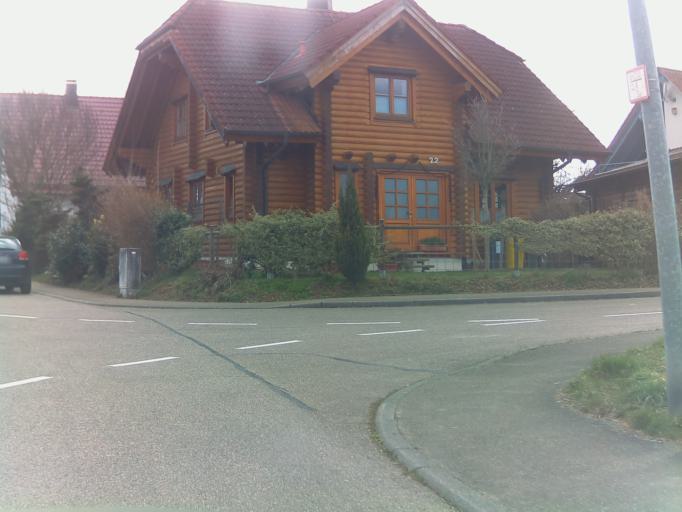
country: DE
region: Baden-Wuerttemberg
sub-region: Regierungsbezirk Stuttgart
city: Alfdorf
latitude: 48.8458
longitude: 9.7095
